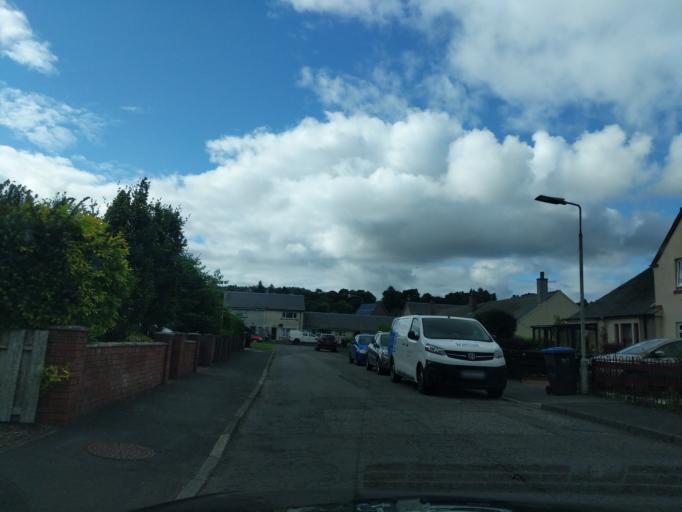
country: GB
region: Scotland
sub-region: The Scottish Borders
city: West Linton
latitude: 55.7506
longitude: -3.3534
